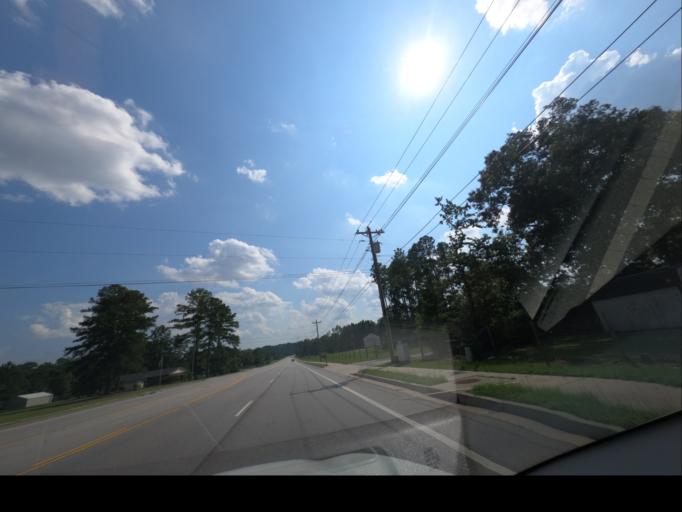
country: US
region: South Carolina
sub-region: Lexington County
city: South Congaree
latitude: 33.9220
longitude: -81.1636
